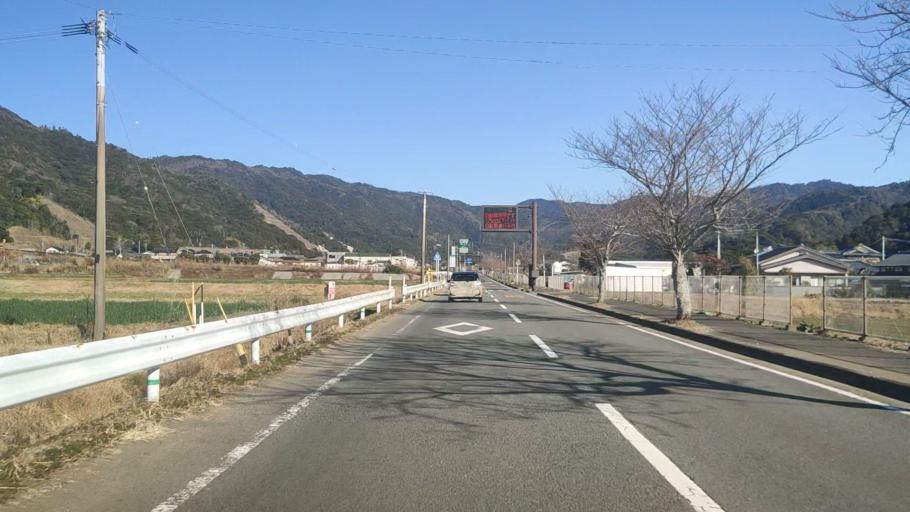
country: JP
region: Miyazaki
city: Nobeoka
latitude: 32.7080
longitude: 131.8192
